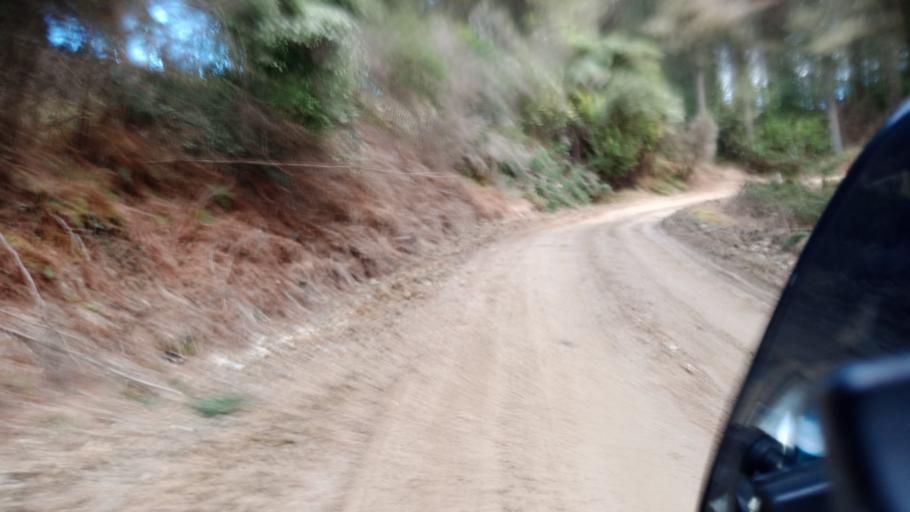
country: NZ
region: Gisborne
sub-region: Gisborne District
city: Gisborne
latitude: -38.8633
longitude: 177.7953
